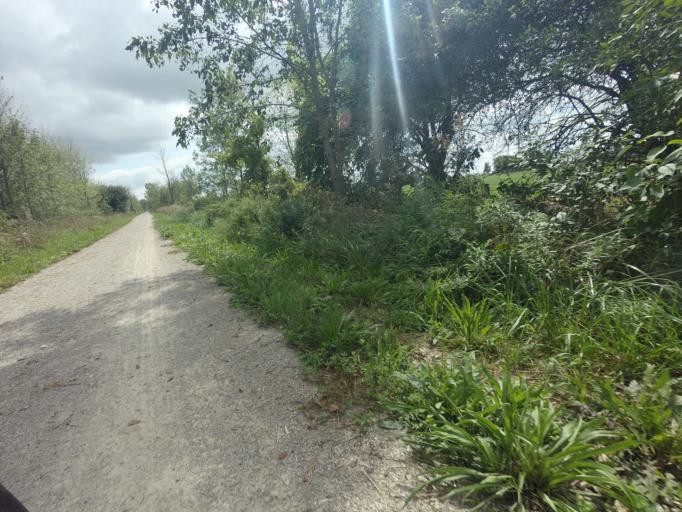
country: CA
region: Ontario
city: North Perth
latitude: 43.5815
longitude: -81.0610
